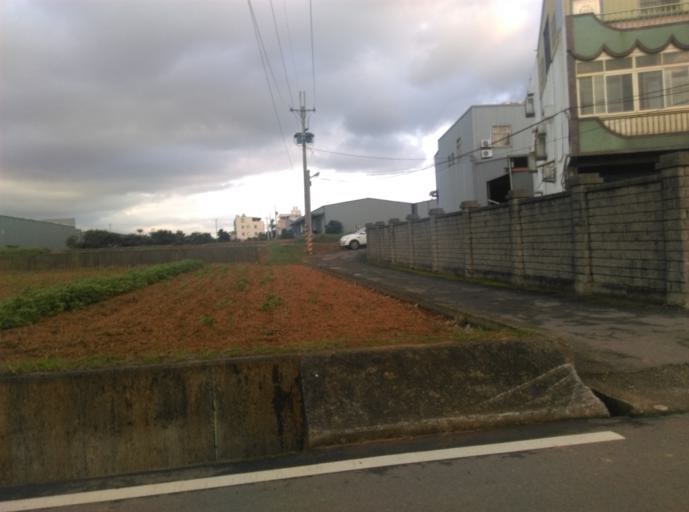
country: TW
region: Taiwan
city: Taoyuan City
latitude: 24.9954
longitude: 121.2512
